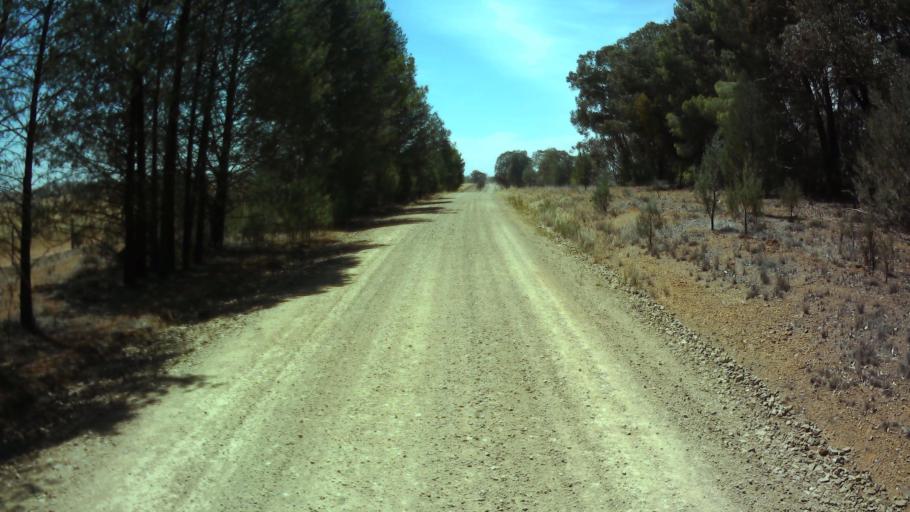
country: AU
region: New South Wales
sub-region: Weddin
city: Grenfell
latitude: -33.9903
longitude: 148.1388
